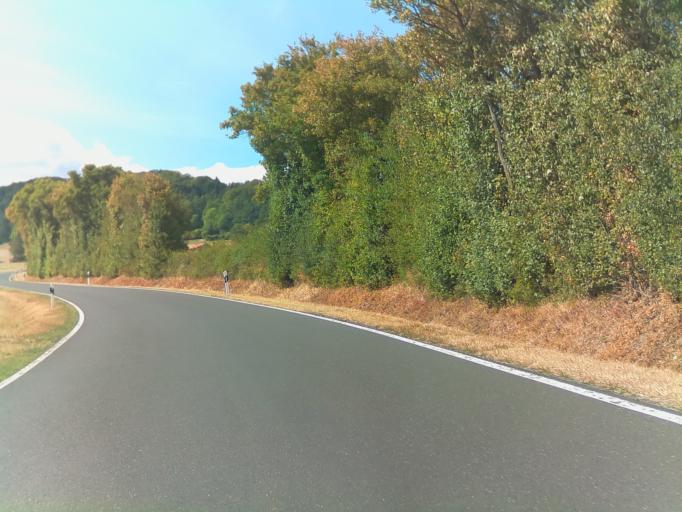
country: DE
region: Bavaria
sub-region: Regierungsbezirk Unterfranken
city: Oberelsbach
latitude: 50.4593
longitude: 10.1235
